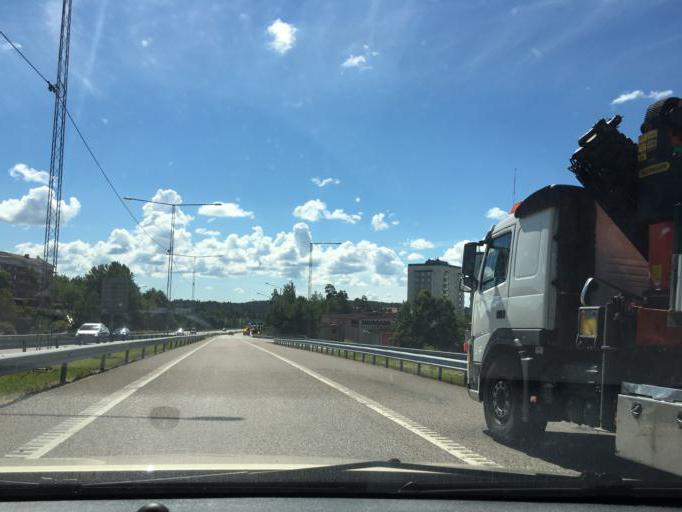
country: SE
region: Stockholm
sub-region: Nacka Kommun
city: Nacka
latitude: 59.3129
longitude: 18.1768
